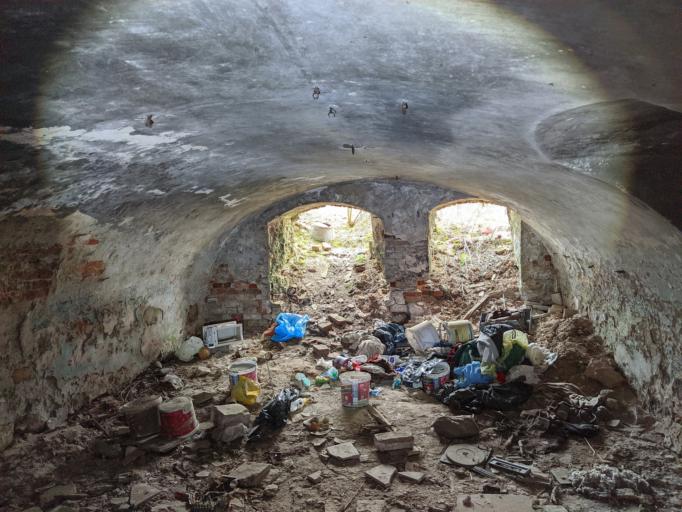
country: PL
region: Lubusz
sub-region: Powiat nowosolski
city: Kozuchow
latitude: 51.7952
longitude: 15.5639
